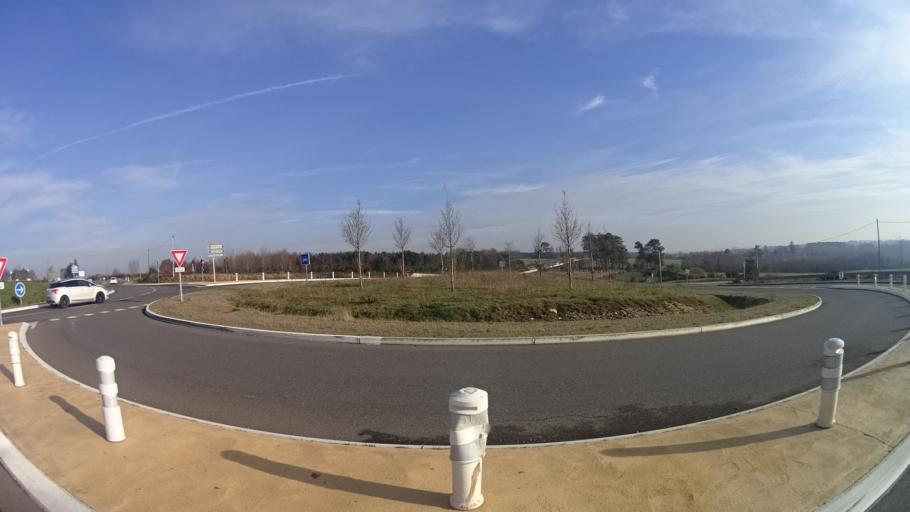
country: FR
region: Brittany
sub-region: Departement du Morbihan
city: Allaire
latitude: 47.6124
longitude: -2.1480
